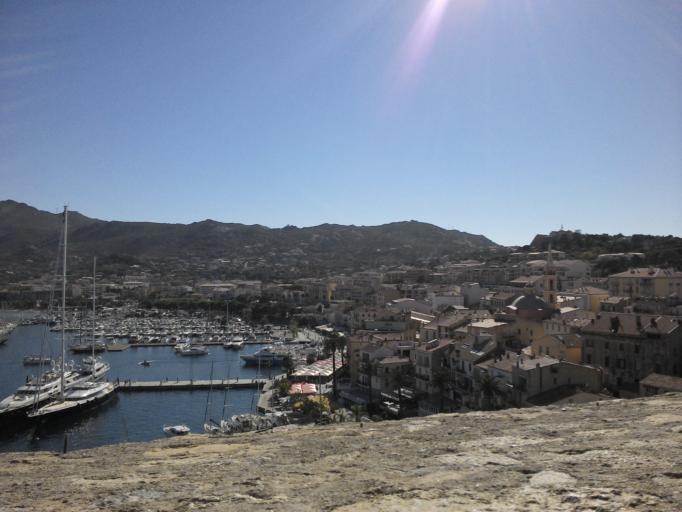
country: FR
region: Corsica
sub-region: Departement de la Haute-Corse
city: Calvi
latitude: 42.5674
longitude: 8.7603
